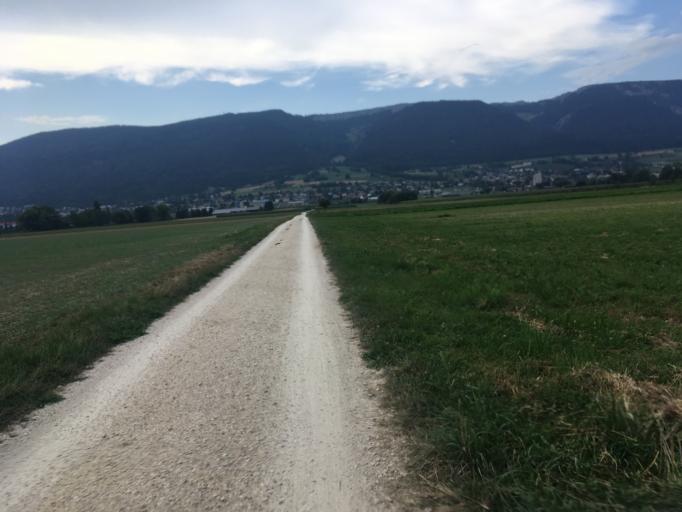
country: CH
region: Bern
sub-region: Seeland District
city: Arch
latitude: 47.1816
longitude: 7.4281
